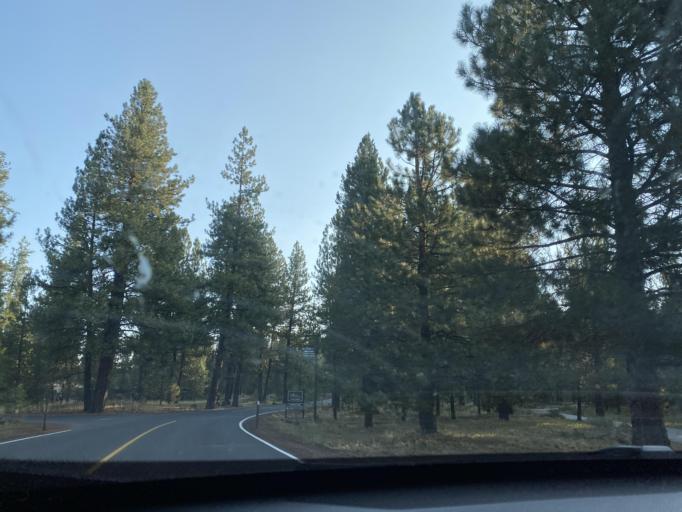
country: US
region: Oregon
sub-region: Deschutes County
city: Sunriver
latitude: 43.8851
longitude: -121.4397
